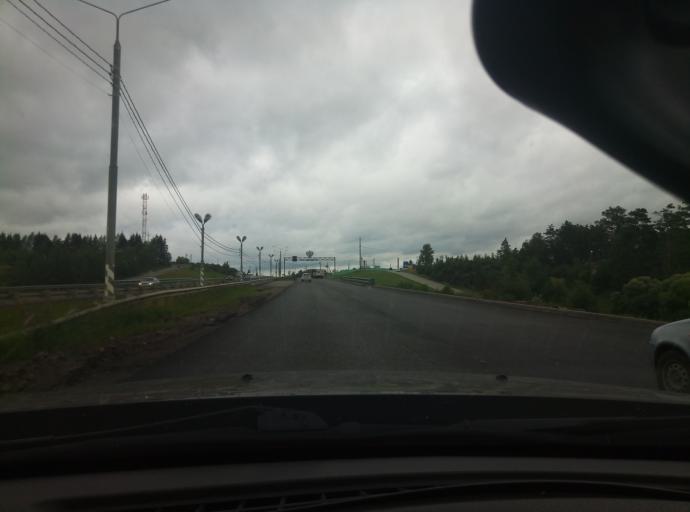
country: RU
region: Tula
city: Zaokskiy
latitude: 54.7237
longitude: 37.5137
